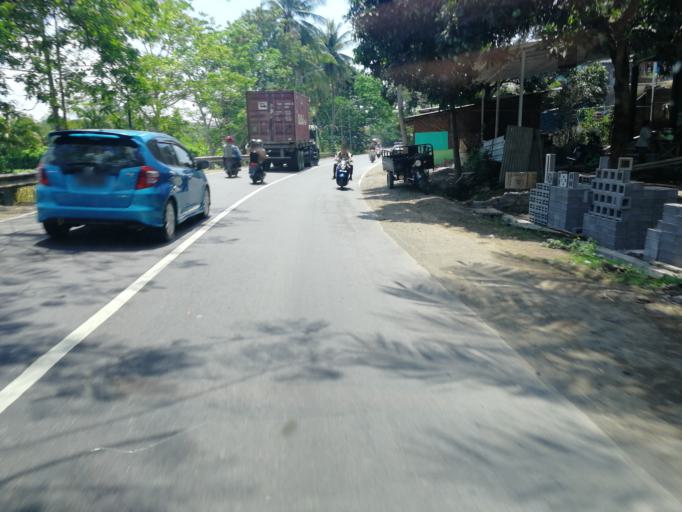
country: ID
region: West Nusa Tenggara
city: Jelateng Timur
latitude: -8.7072
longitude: 116.0817
